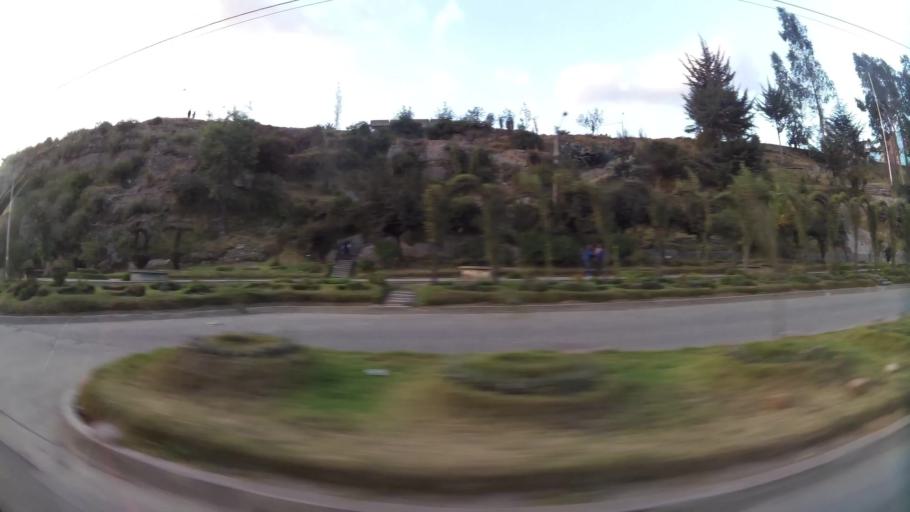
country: PE
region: Junin
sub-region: Provincia de Huancayo
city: Pilcomay
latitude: -12.0529
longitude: -75.2384
